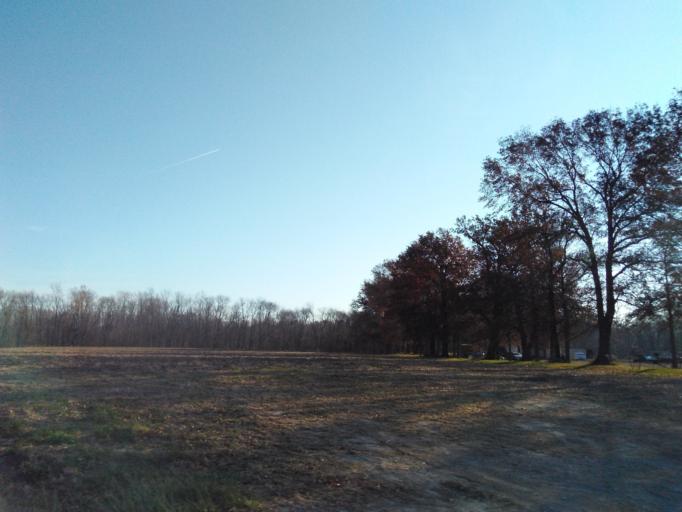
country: US
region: Illinois
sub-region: Madison County
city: Saint Jacob
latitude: 38.7318
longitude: -89.8012
